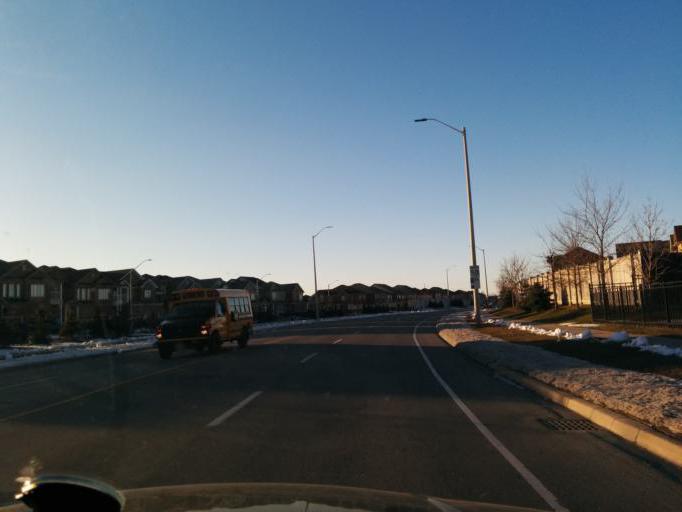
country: CA
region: Ontario
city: Mississauga
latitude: 43.5947
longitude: -79.6595
